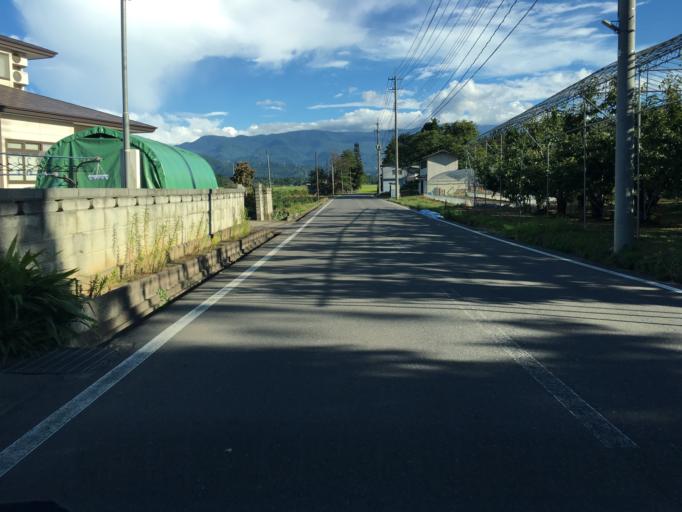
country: JP
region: Yamagata
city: Yonezawa
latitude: 37.8906
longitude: 140.0938
